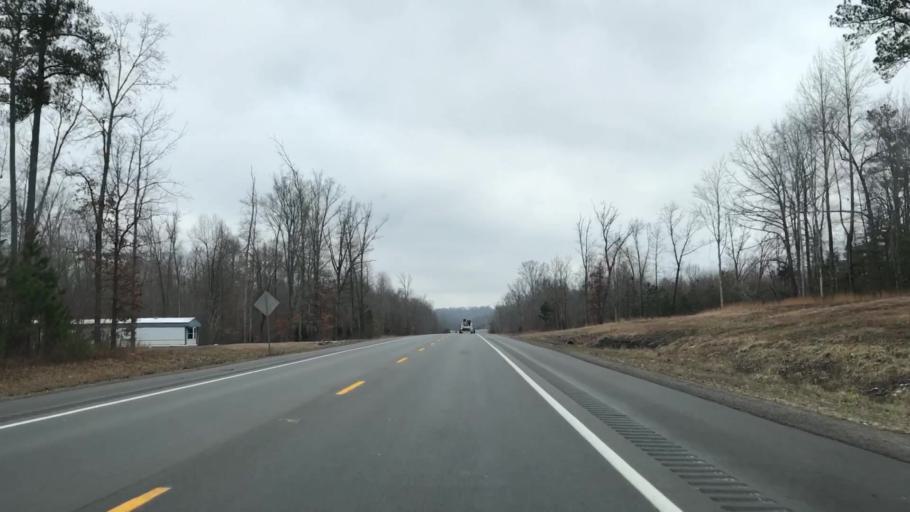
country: US
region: Kentucky
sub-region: Adair County
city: Columbia
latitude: 37.0472
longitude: -85.3652
